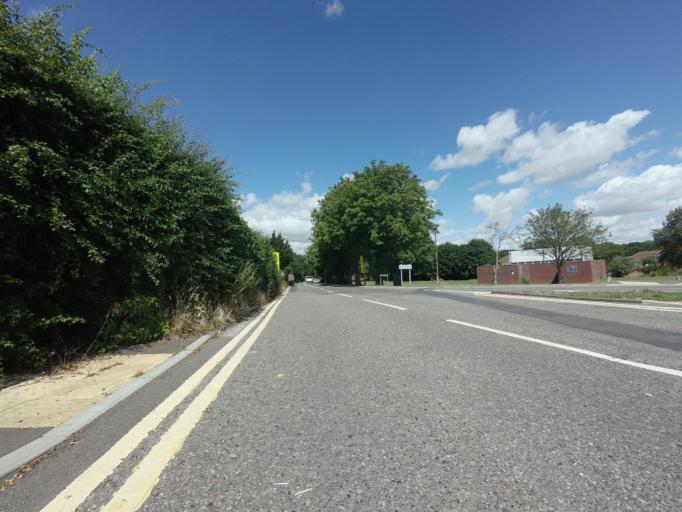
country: GB
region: England
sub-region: Medway
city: Cooling
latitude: 51.4187
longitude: 0.5272
